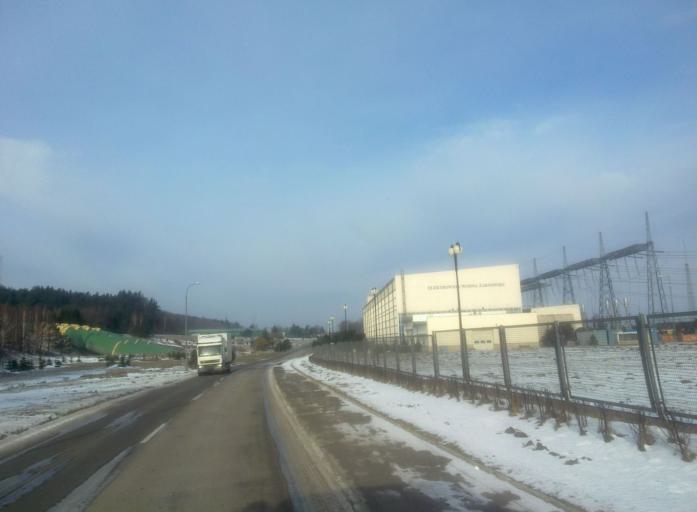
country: PL
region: Pomeranian Voivodeship
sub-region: Powiat wejherowski
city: Gniewino
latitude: 54.7202
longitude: 18.0843
